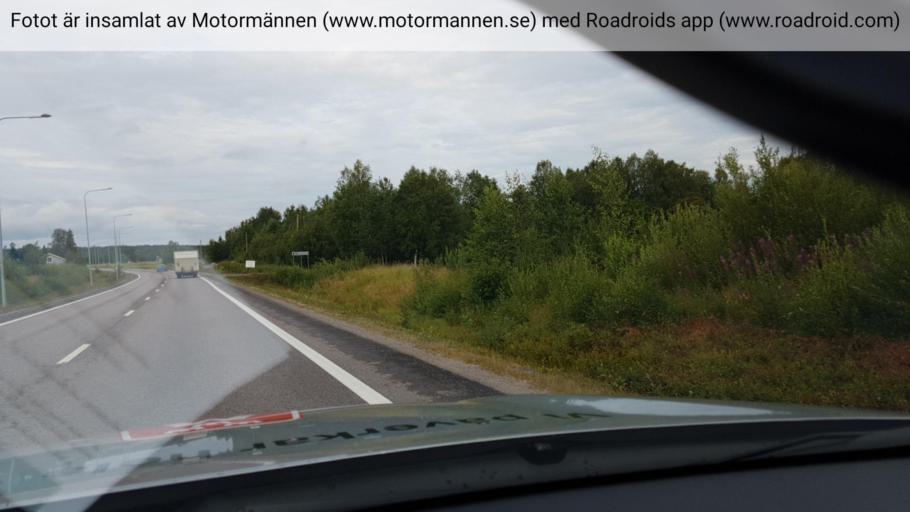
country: SE
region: Norrbotten
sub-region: Lulea Kommun
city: Bergnaset
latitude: 65.5813
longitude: 22.0575
